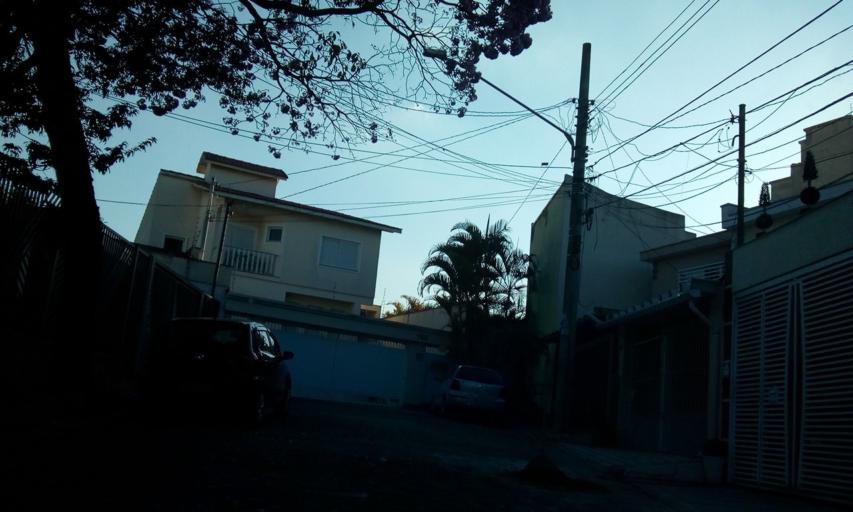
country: BR
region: Sao Paulo
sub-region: Sao Paulo
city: Sao Paulo
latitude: -23.4917
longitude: -46.6137
